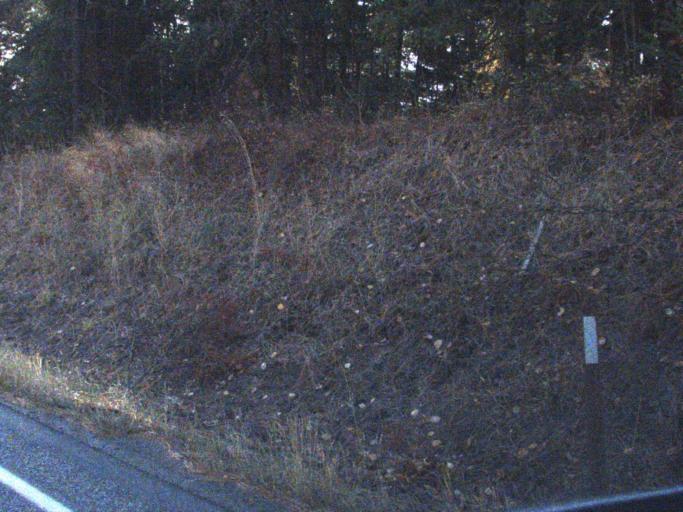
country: US
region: Washington
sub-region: Stevens County
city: Kettle Falls
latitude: 48.8196
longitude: -117.9201
